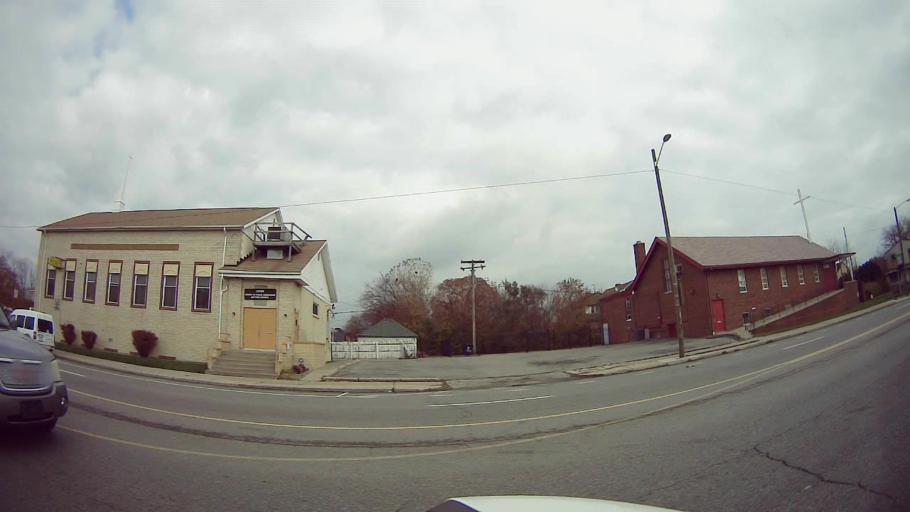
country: US
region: Michigan
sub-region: Wayne County
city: Highland Park
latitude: 42.3890
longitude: -83.1194
